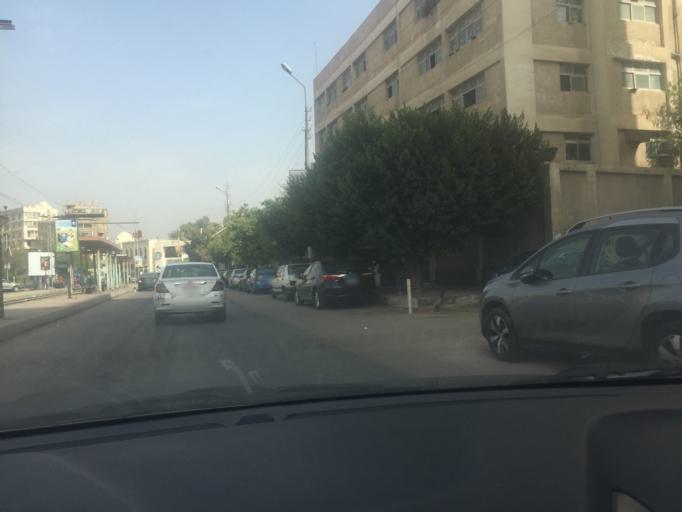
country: EG
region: Muhafazat al Qahirah
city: Cairo
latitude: 30.0846
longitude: 31.3478
